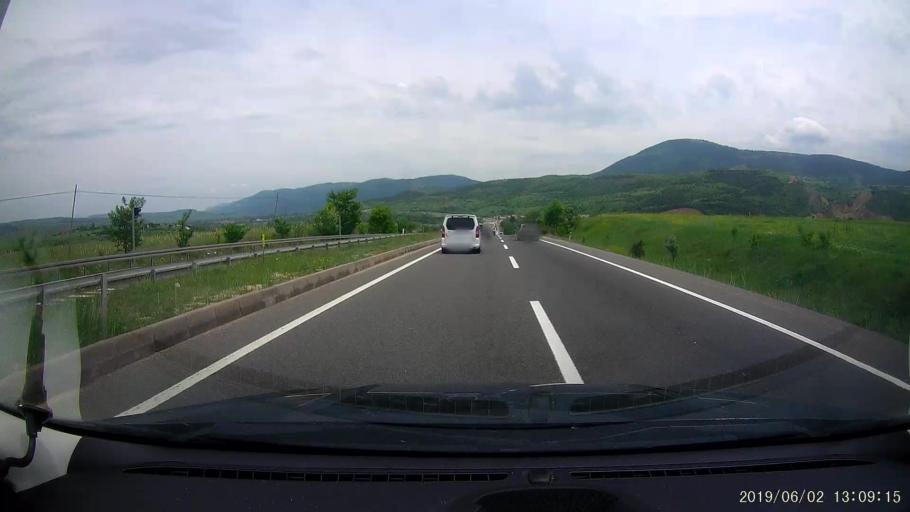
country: TR
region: Karabuk
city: Gozyeri
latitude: 40.8708
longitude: 32.5849
